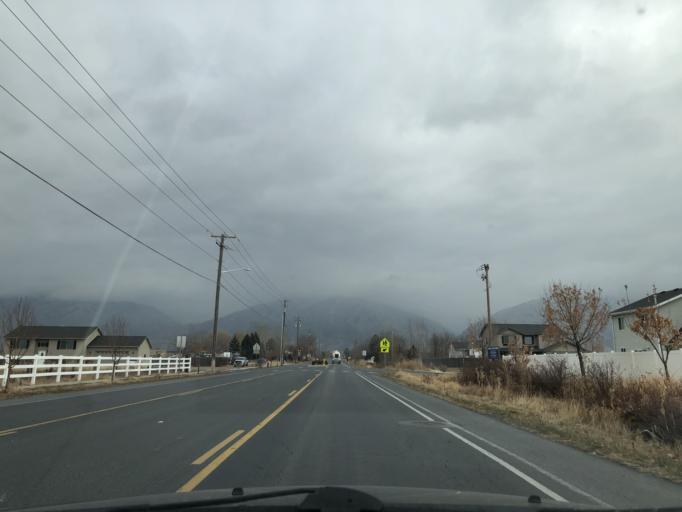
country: US
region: Utah
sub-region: Cache County
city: Nibley
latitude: 41.6750
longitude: -111.8656
